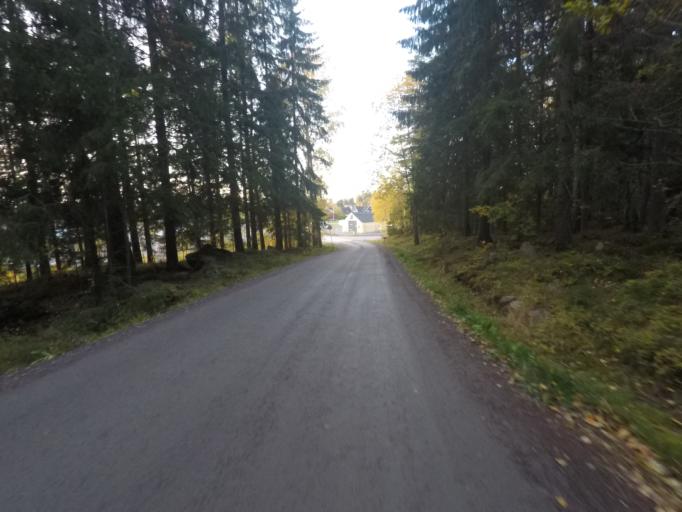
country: SE
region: OErebro
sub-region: Karlskoga Kommun
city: Karlskoga
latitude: 59.3022
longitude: 14.5009
